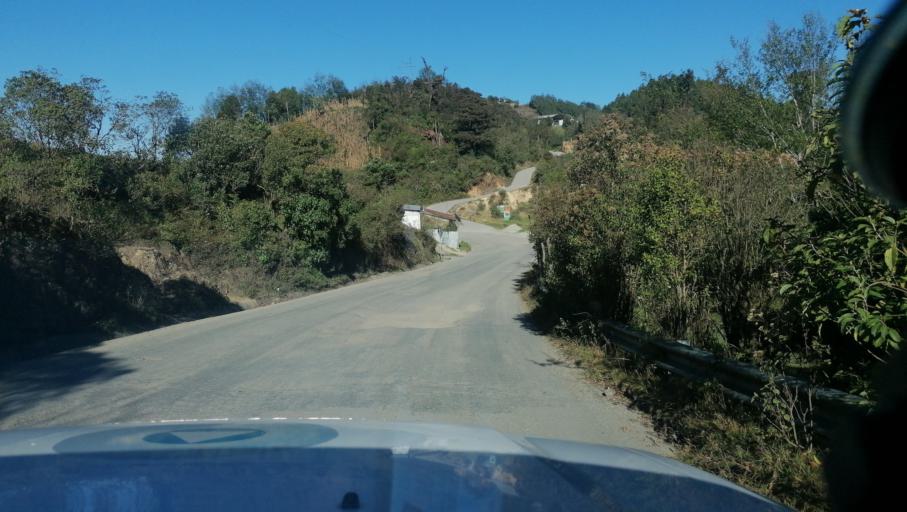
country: MX
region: Chiapas
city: Motozintla de Mendoza
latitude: 15.2657
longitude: -92.2207
